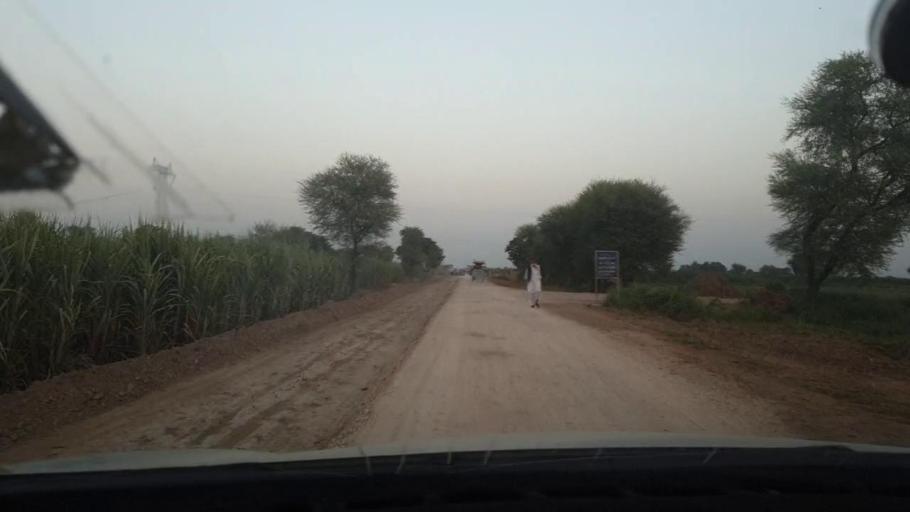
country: PK
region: Sindh
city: Bhit Shah
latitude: 25.7530
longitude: 68.5614
